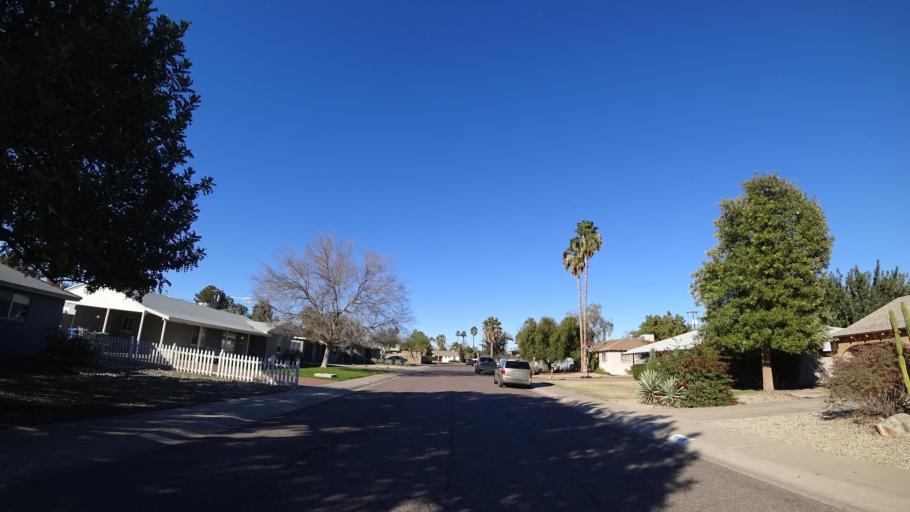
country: US
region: Arizona
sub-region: Maricopa County
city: Phoenix
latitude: 33.5215
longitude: -112.0528
